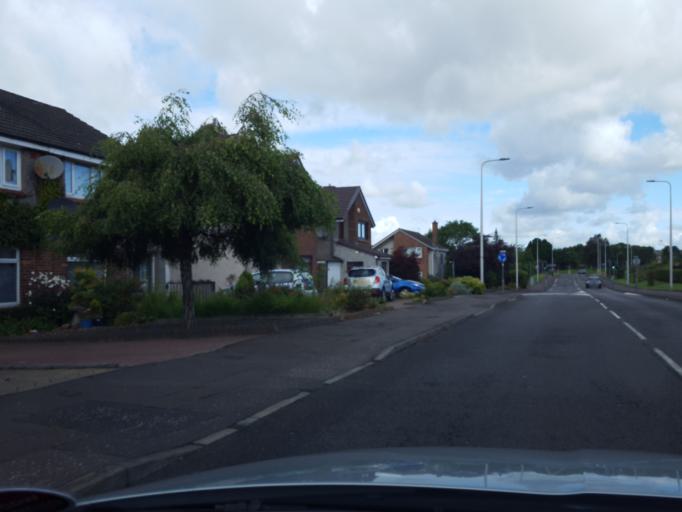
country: GB
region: Scotland
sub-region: Fife
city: Rosyth
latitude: 56.0576
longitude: -3.4155
